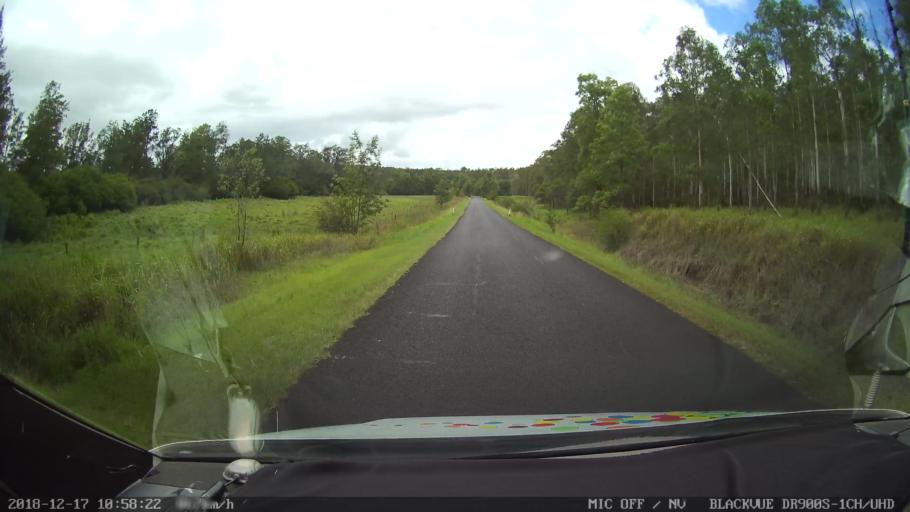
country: AU
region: New South Wales
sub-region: Richmond Valley
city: Casino
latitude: -28.8235
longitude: 152.6039
